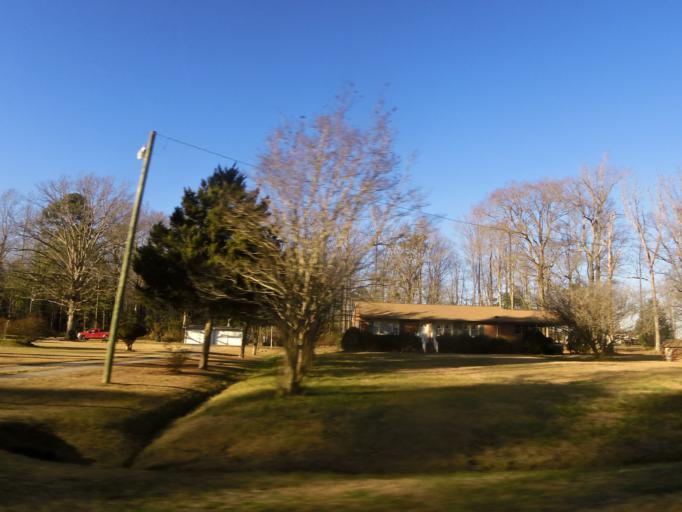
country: US
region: Virginia
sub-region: City of Franklin
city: Franklin
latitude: 36.6523
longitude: -76.8380
